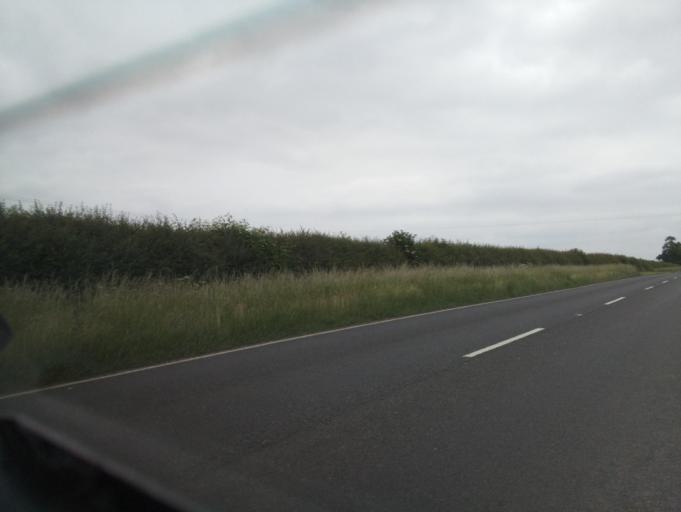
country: GB
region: England
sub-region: District of Rutland
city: Exton
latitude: 52.6671
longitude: -0.6253
